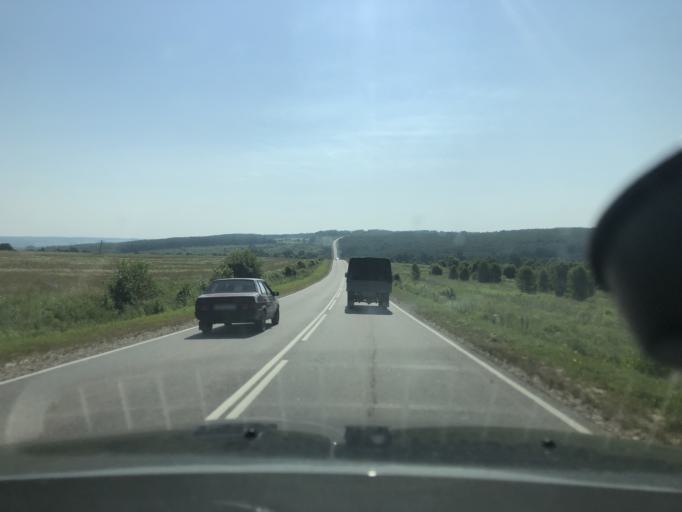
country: RU
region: Tula
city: Dubna
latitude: 54.1324
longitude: 37.0313
